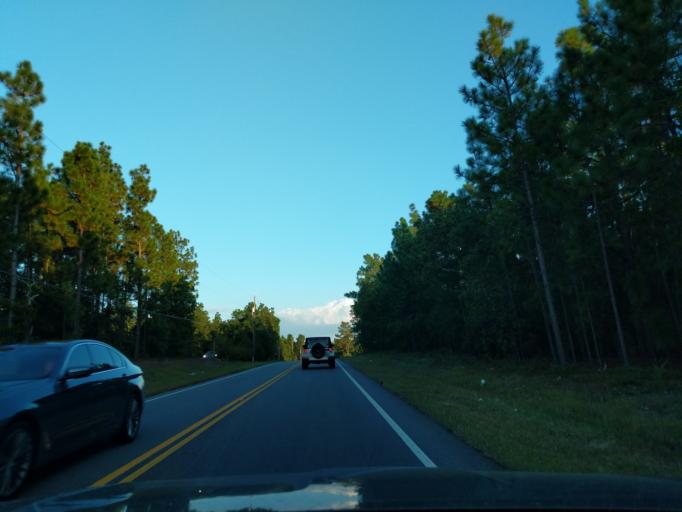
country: US
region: South Carolina
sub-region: Aiken County
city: Burnettown
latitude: 33.5387
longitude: -81.8676
